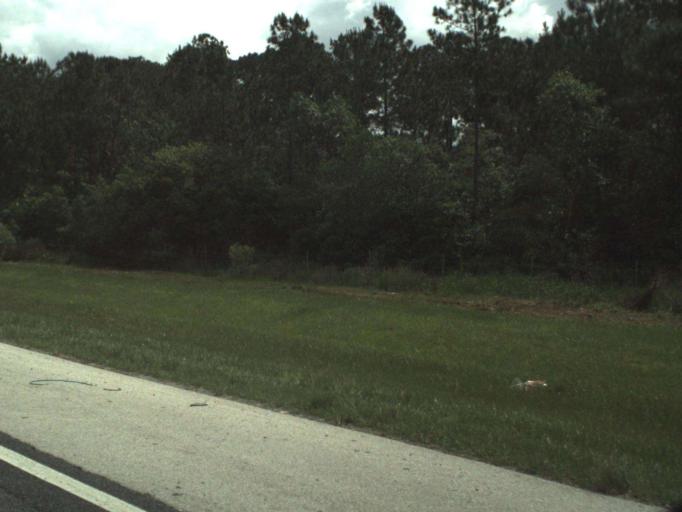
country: US
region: Florida
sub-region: Volusia County
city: Lake Helen
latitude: 28.9909
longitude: -81.2462
